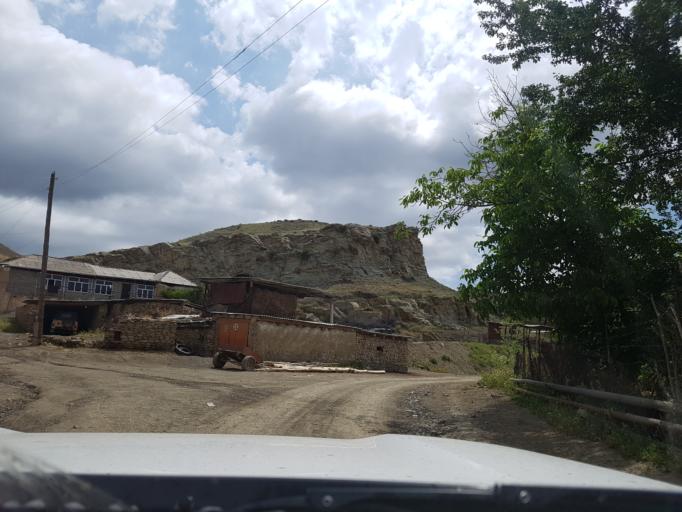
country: TM
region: Ahal
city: Baharly
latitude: 38.2039
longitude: 57.0012
